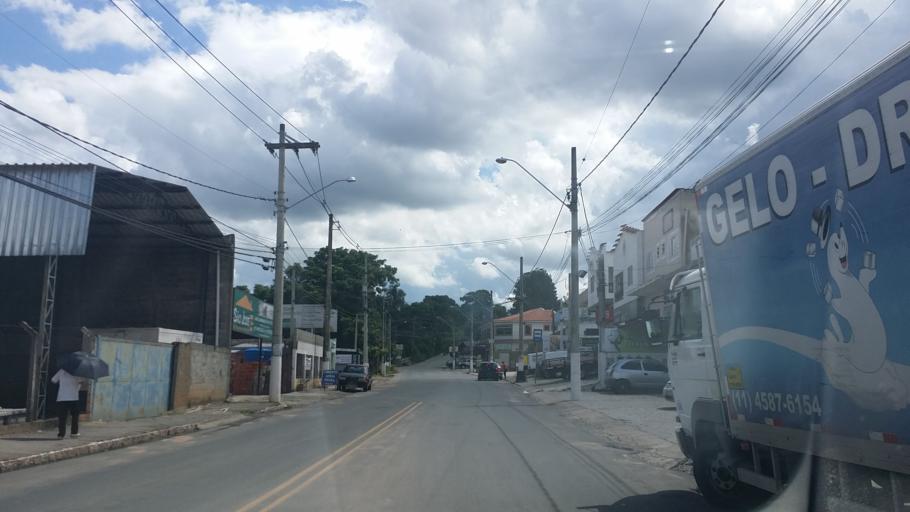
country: BR
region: Sao Paulo
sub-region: Itupeva
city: Itupeva
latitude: -23.1549
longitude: -47.0619
